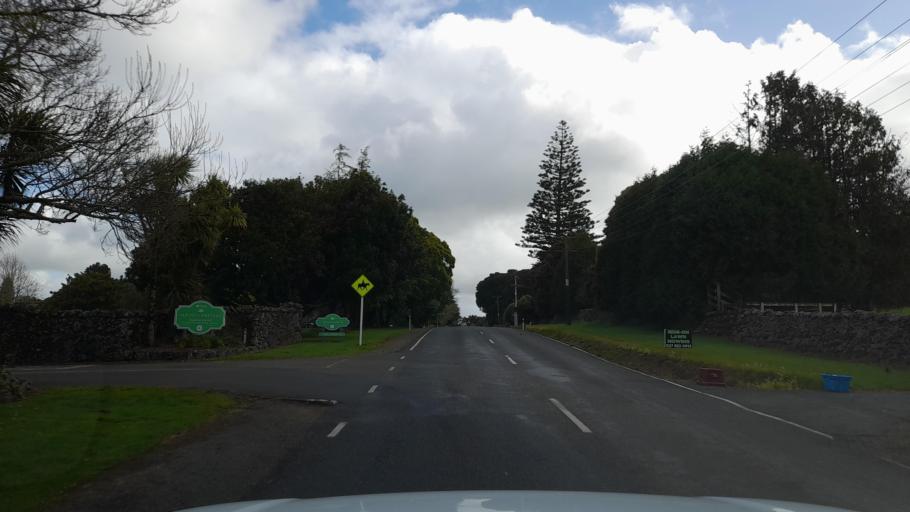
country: NZ
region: Northland
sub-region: Whangarei
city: Maungatapere
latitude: -35.7441
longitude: 174.2575
